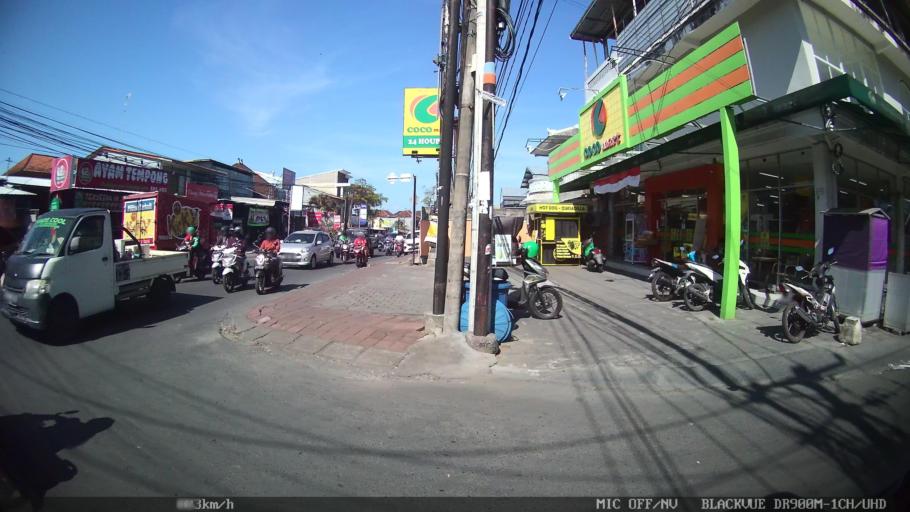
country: ID
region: Bali
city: Denpasar
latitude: -8.6472
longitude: 115.1766
